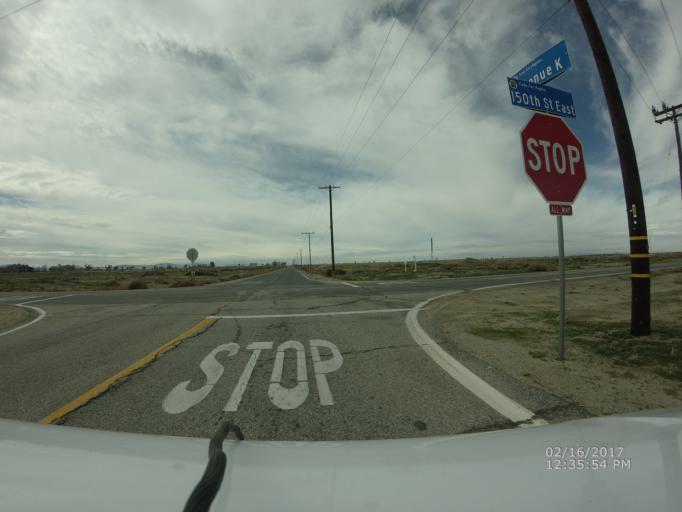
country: US
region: California
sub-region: Los Angeles County
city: Lake Los Angeles
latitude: 34.6754
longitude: -117.8630
